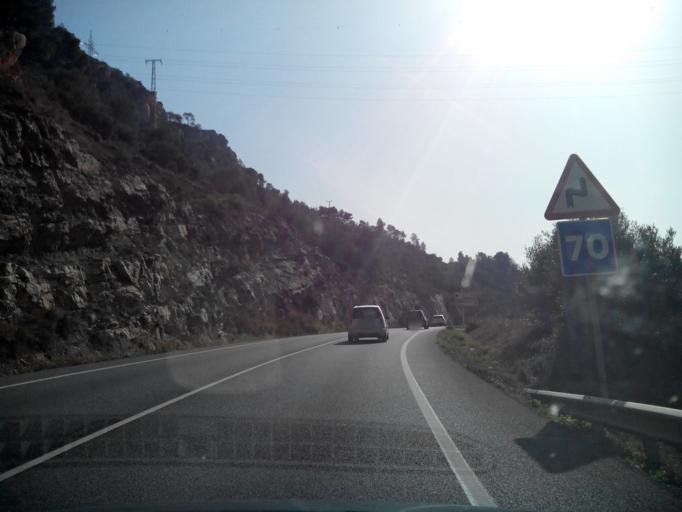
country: ES
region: Catalonia
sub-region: Provincia de Tarragona
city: Alcover
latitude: 41.3126
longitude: 1.1887
